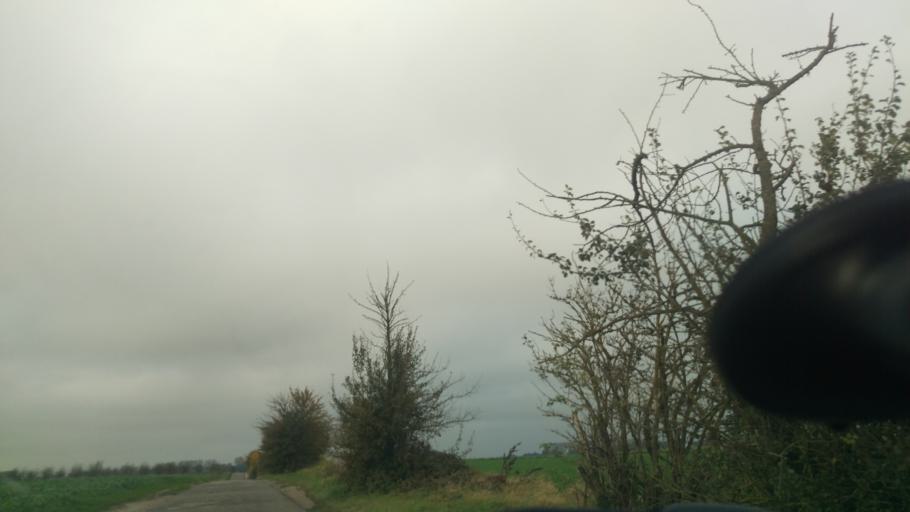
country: PL
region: West Pomeranian Voivodeship
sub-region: Powiat pyrzycki
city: Przelewice
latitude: 53.0594
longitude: 15.1082
